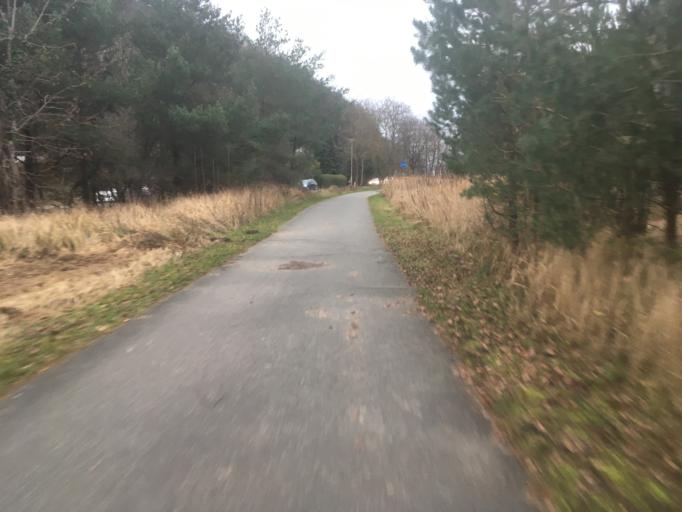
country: DE
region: Mecklenburg-Vorpommern
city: Sagard
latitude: 54.4771
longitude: 13.5733
